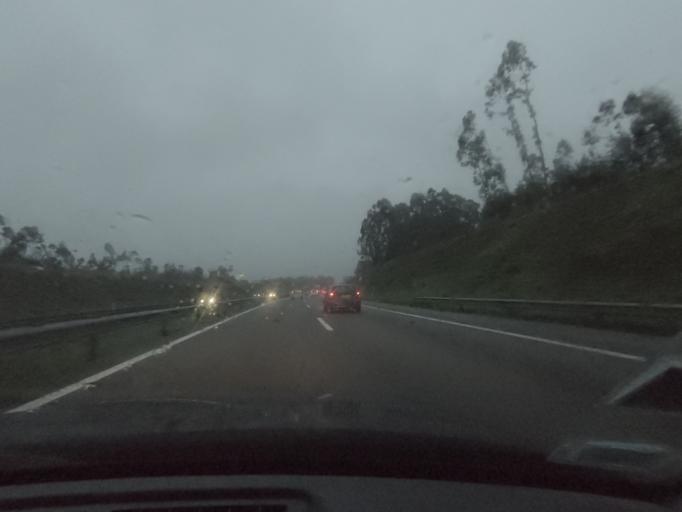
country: PT
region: Porto
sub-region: Matosinhos
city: Santa Cruz do Bispo
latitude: 41.2470
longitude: -8.6952
